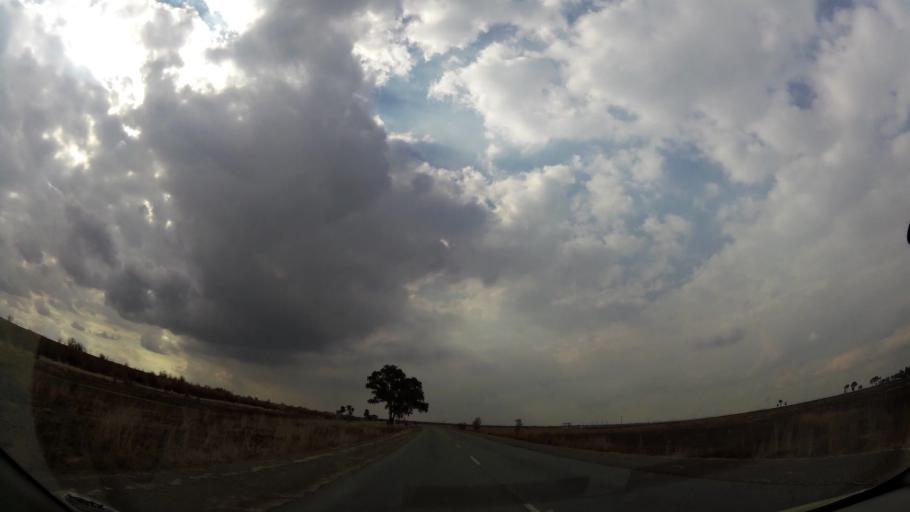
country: ZA
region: Orange Free State
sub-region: Fezile Dabi District Municipality
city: Sasolburg
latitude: -26.8802
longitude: 27.8860
